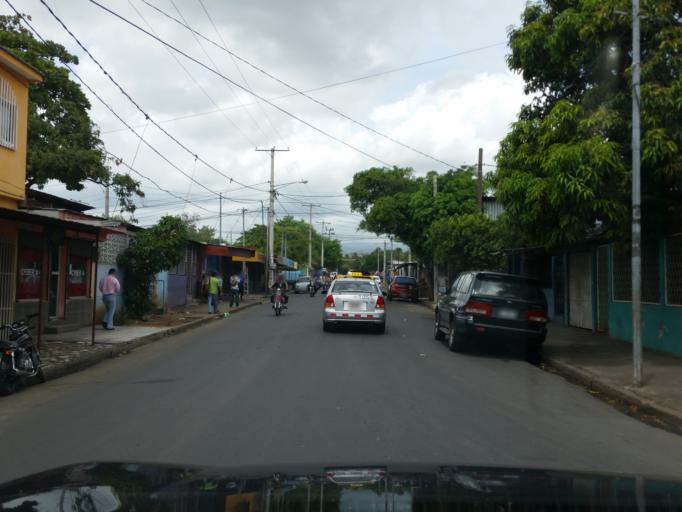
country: NI
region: Managua
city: Managua
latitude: 12.1372
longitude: -86.2536
